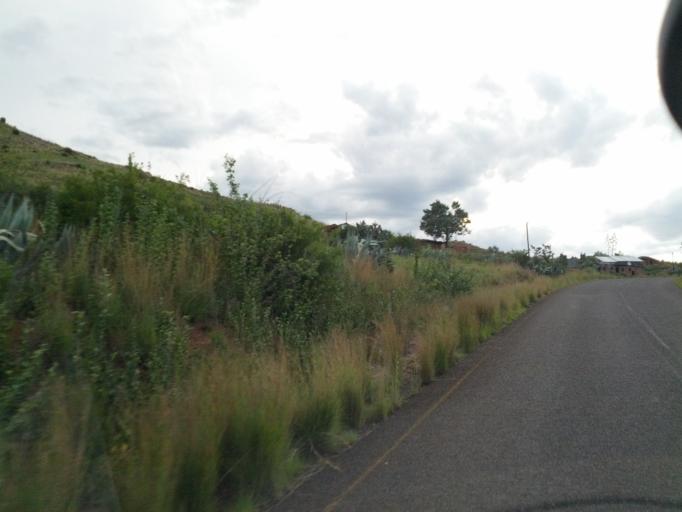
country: LS
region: Qacha's Nek
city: Qacha's Nek
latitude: -30.0666
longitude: 28.5385
